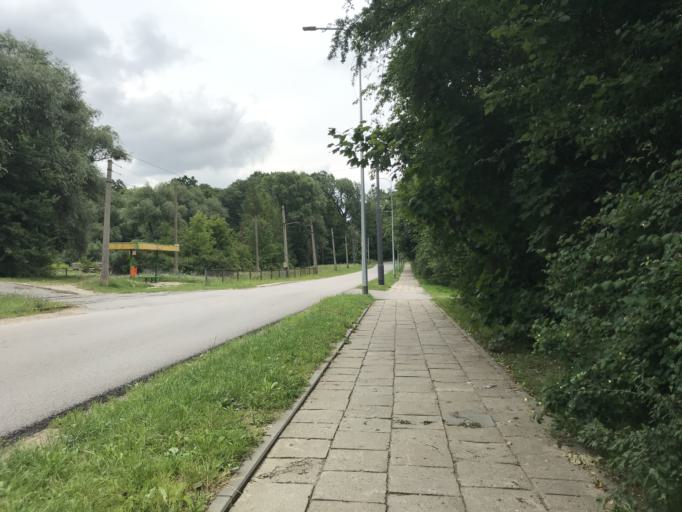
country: PL
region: Warmian-Masurian Voivodeship
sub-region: Powiat elblaski
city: Elblag
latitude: 54.1762
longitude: 19.4340
